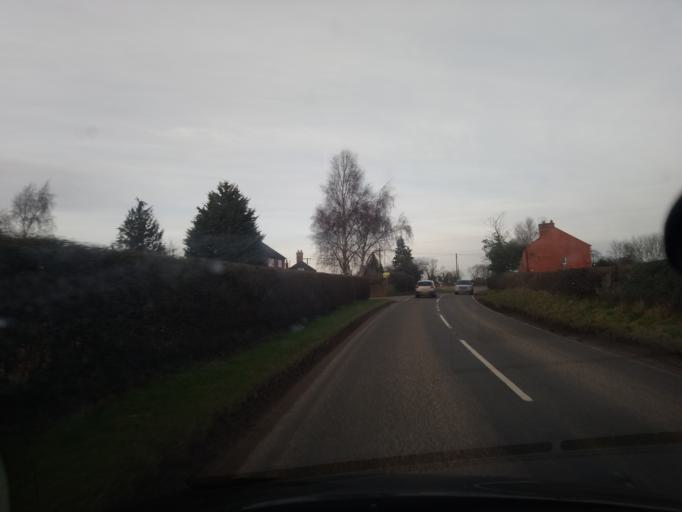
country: GB
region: England
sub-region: Shropshire
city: Wem
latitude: 52.8860
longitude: -2.7124
